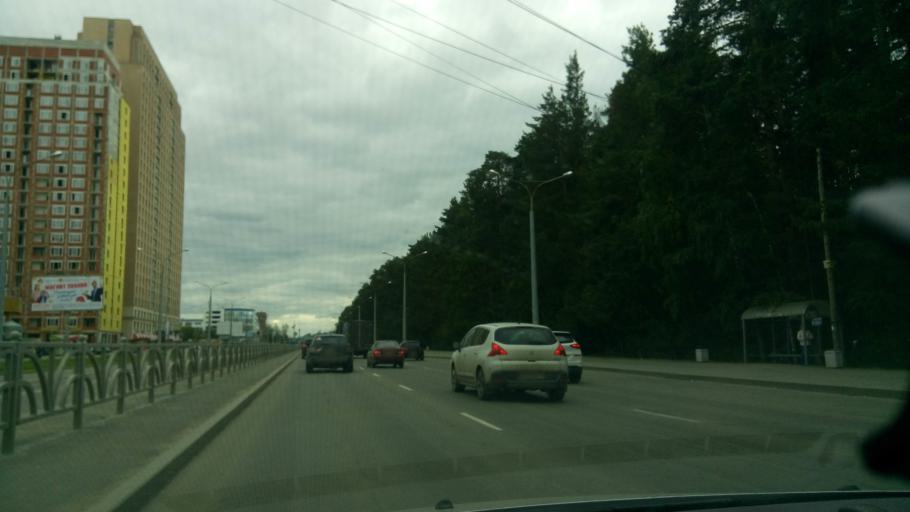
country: RU
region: Sverdlovsk
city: Sovkhoznyy
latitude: 56.7794
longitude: 60.5463
